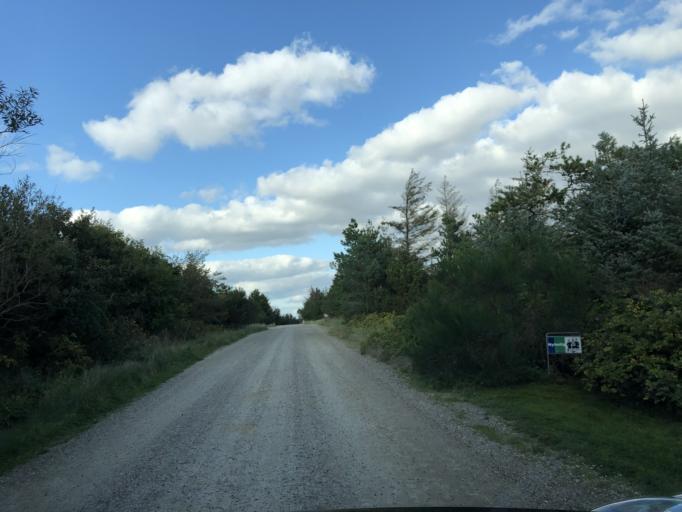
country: DK
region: Central Jutland
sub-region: Holstebro Kommune
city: Ulfborg
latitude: 56.3215
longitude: 8.1385
